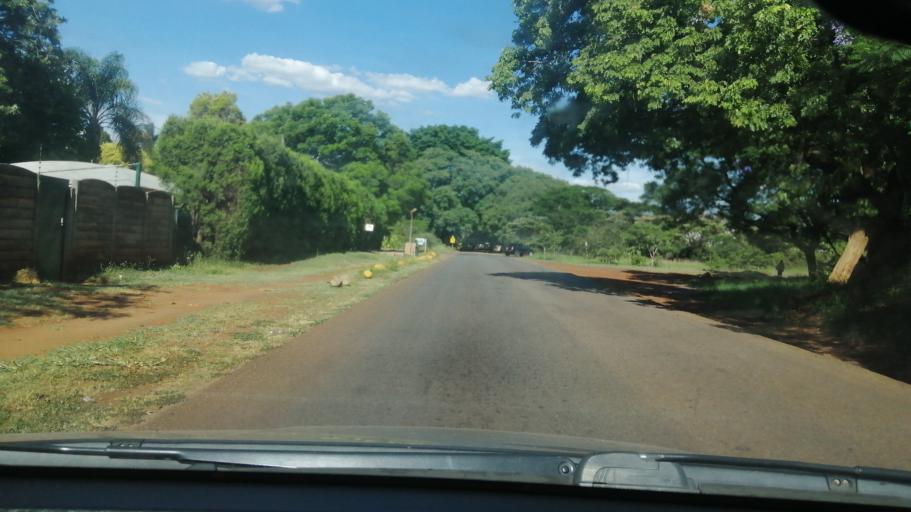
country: ZW
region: Harare
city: Harare
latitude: -17.7946
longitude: 31.0560
